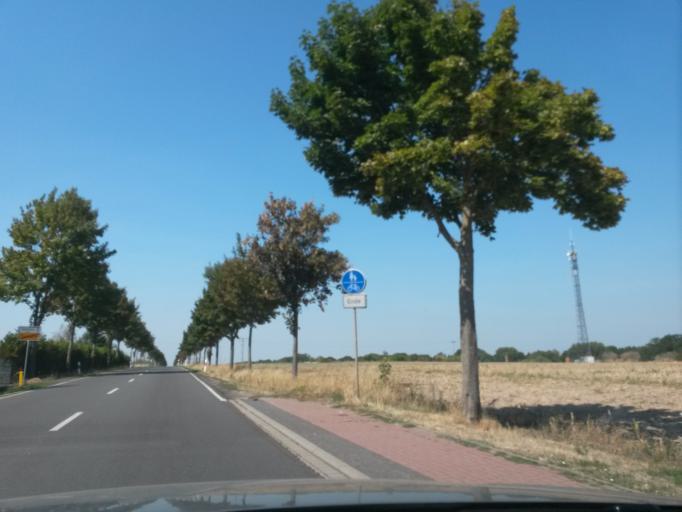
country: DE
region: Saxony-Anhalt
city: Tucheim
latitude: 52.2935
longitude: 12.1734
